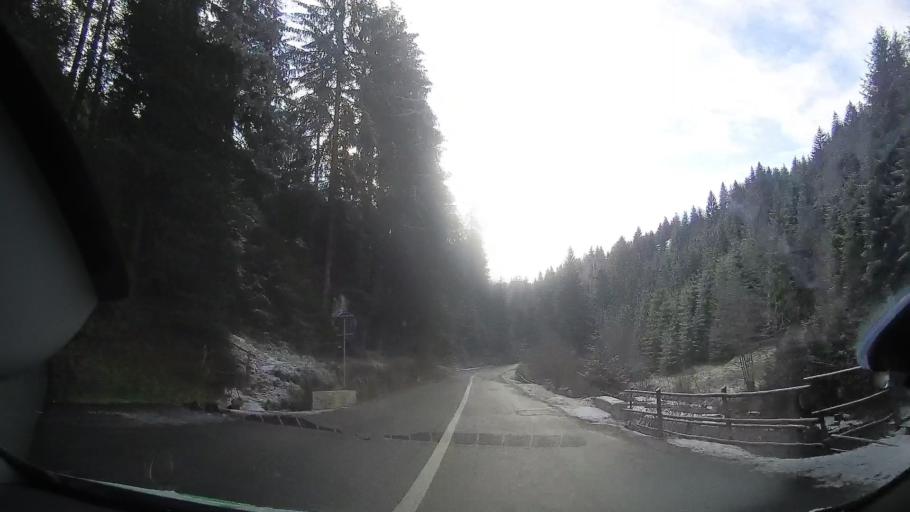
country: RO
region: Alba
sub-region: Comuna Horea
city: Horea
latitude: 46.4914
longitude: 22.9620
